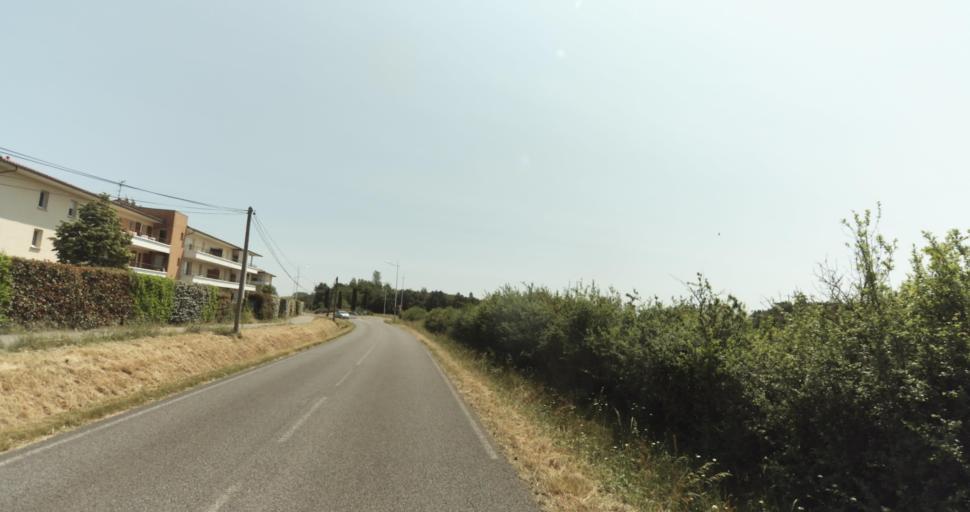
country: FR
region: Midi-Pyrenees
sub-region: Departement de la Haute-Garonne
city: La Salvetat-Saint-Gilles
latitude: 43.5993
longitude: 1.2611
